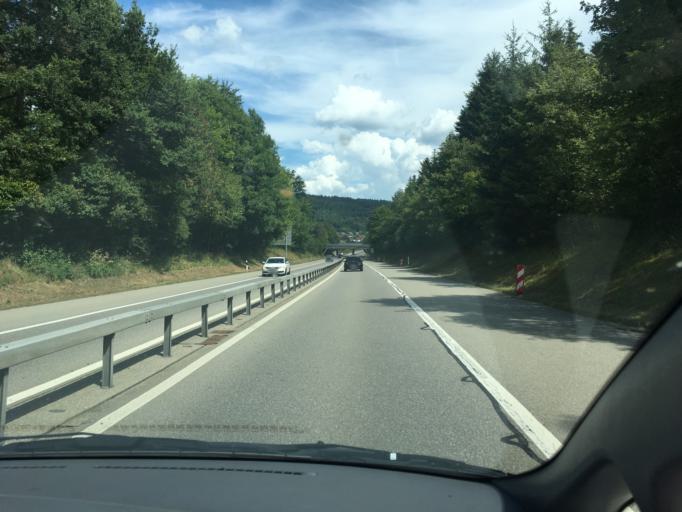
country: CH
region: Bern
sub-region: Bern-Mittelland District
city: Muri
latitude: 46.9260
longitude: 7.5119
